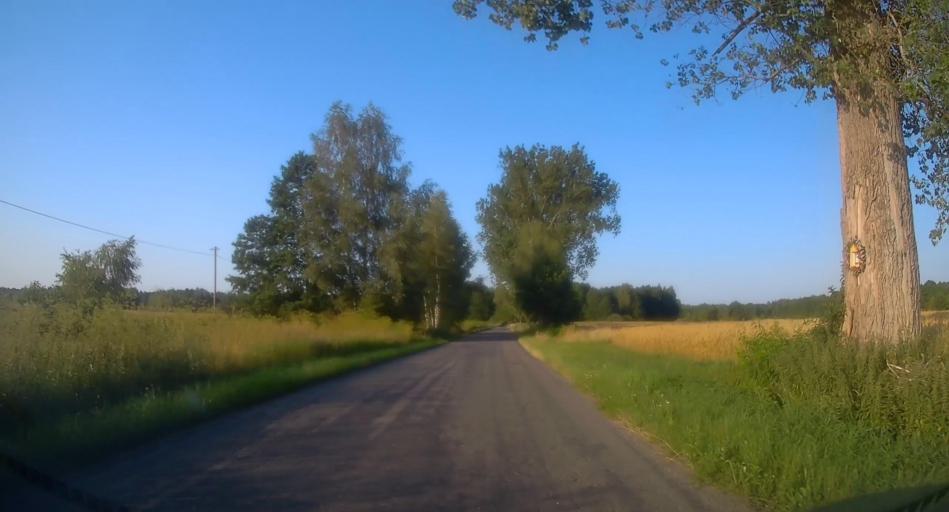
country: PL
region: Lodz Voivodeship
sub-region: Powiat skierniewicki
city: Kaweczyn Nowy
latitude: 51.8870
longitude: 20.2855
